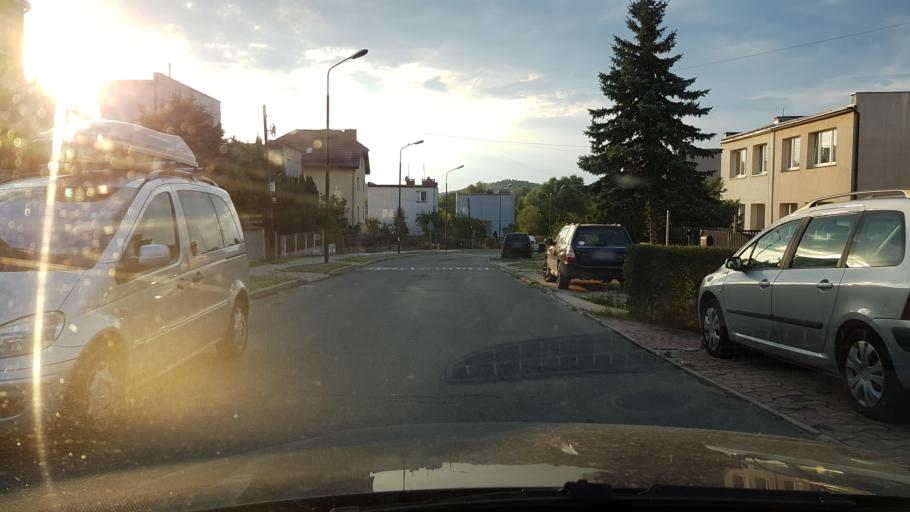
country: PL
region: Lower Silesian Voivodeship
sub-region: Jelenia Gora
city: Jelenia Gora
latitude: 50.8872
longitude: 15.7315
